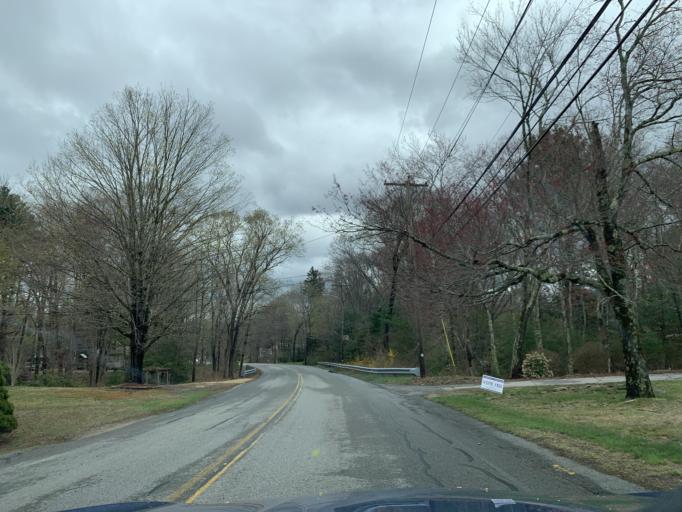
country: US
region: Massachusetts
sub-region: Bristol County
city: Norton
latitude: 41.9599
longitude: -71.2372
